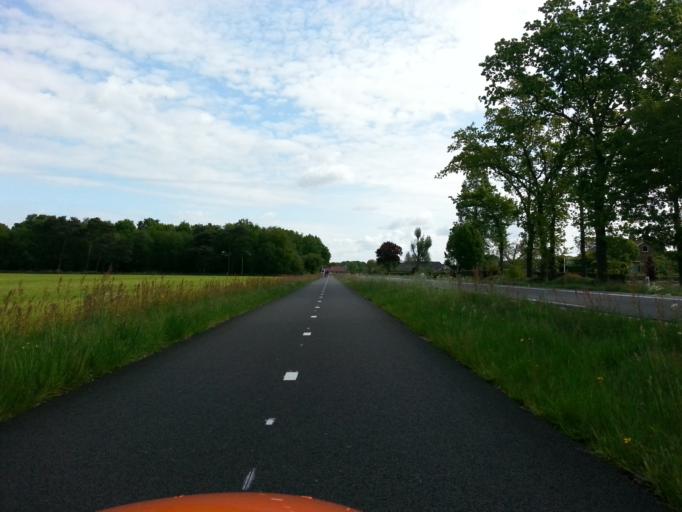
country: NL
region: Gelderland
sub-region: Gemeente Barneveld
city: Terschuur
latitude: 52.1079
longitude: 5.5270
